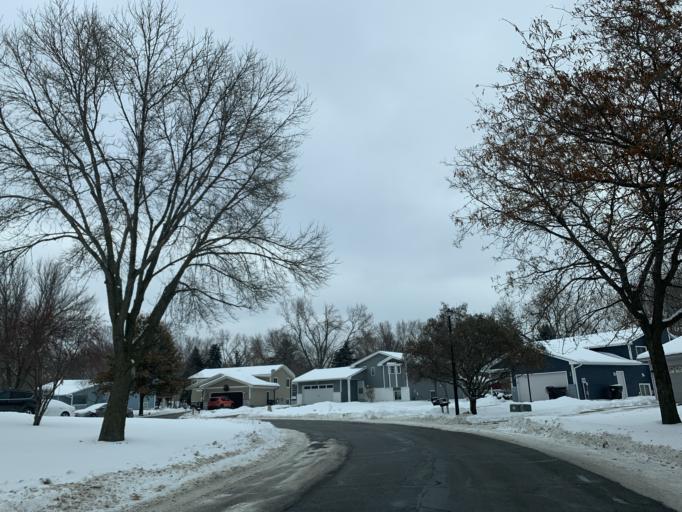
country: US
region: Minnesota
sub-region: Anoka County
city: Coon Rapids
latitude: 45.1647
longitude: -93.2816
